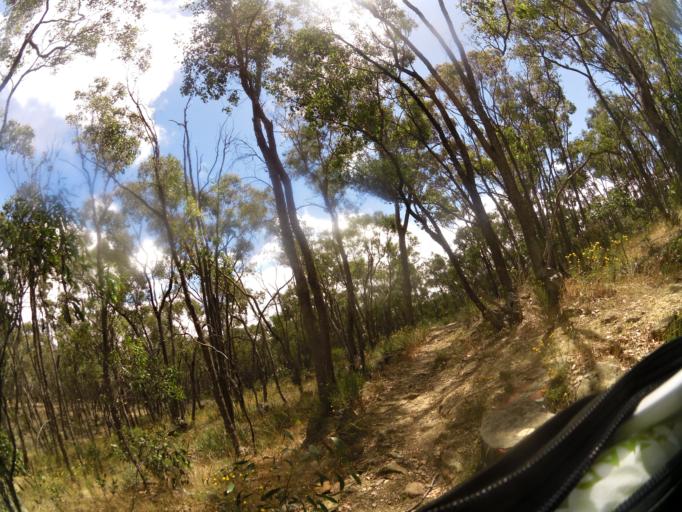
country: AU
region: Victoria
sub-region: Mount Alexander
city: Castlemaine
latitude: -37.0721
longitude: 144.2608
